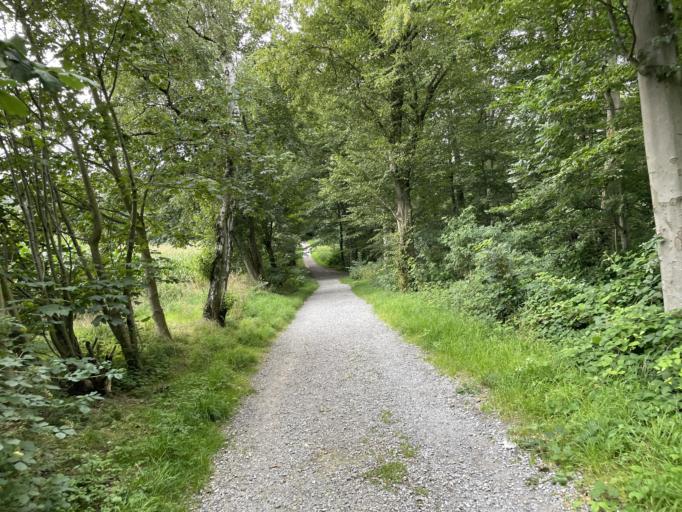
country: DE
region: North Rhine-Westphalia
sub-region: Regierungsbezirk Dusseldorf
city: Heiligenhaus
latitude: 51.3747
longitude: 6.9545
